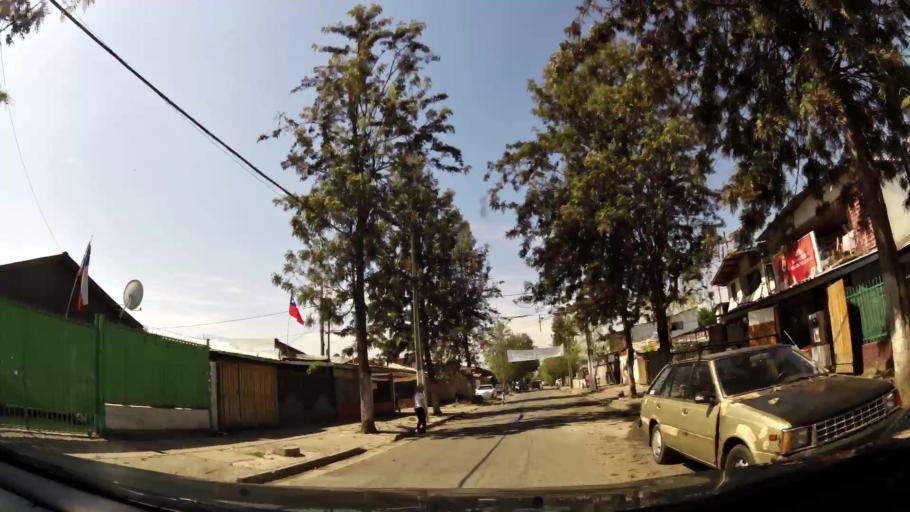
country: CL
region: Santiago Metropolitan
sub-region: Provincia de Santiago
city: La Pintana
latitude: -33.5934
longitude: -70.6243
